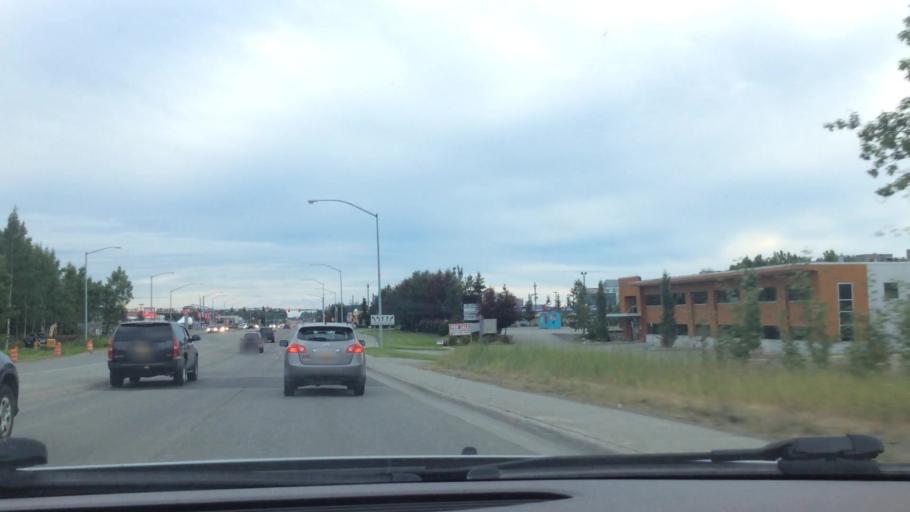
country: US
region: Alaska
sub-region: Anchorage Municipality
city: Anchorage
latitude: 61.1808
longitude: -149.8625
